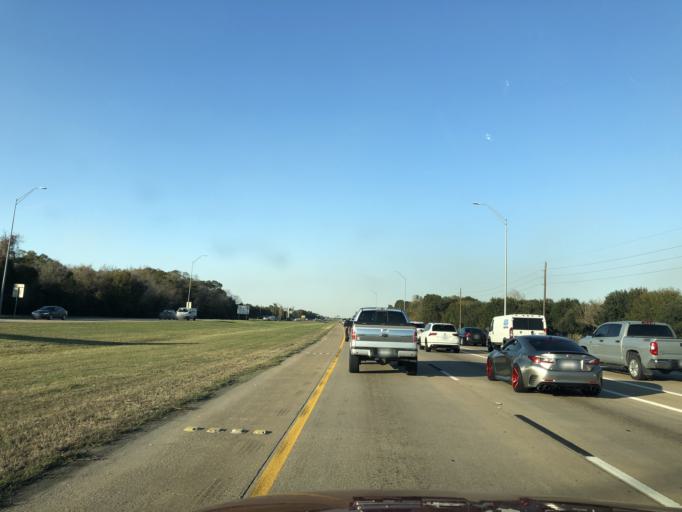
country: US
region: Texas
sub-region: Fort Bend County
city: Cinco Ranch
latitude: 29.7181
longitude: -95.7726
